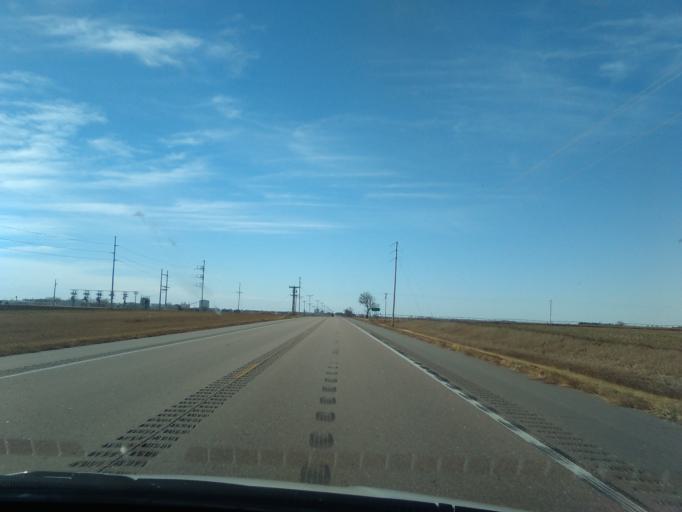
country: US
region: Nebraska
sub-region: Clay County
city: Harvard
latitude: 40.5824
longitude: -98.2200
